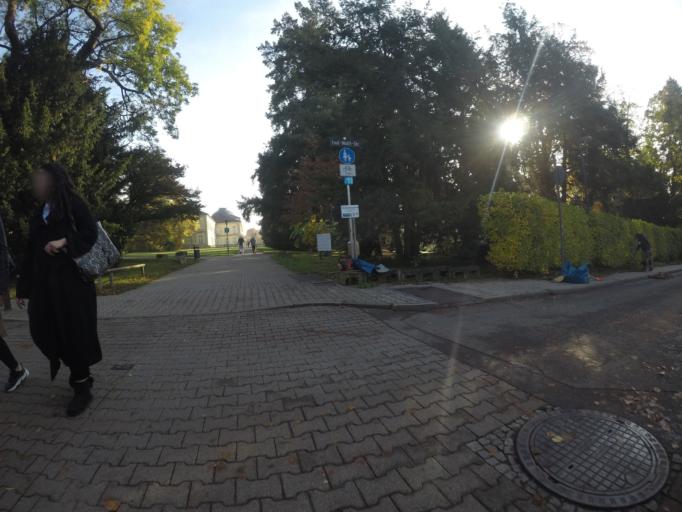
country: DE
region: Baden-Wuerttemberg
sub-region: Regierungsbezirk Stuttgart
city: Ostfildern
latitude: 48.7116
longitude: 9.2114
